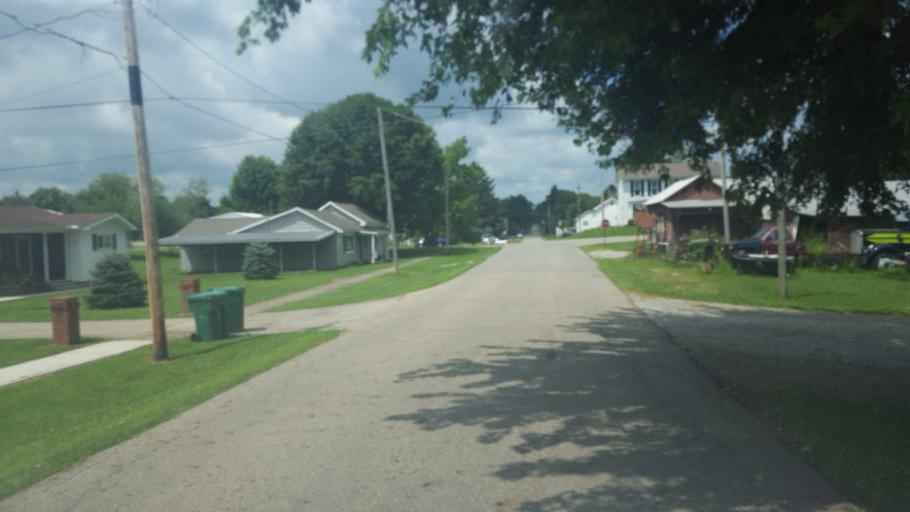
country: US
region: Ohio
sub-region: Ross County
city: Kingston
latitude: 39.4651
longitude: -82.7447
